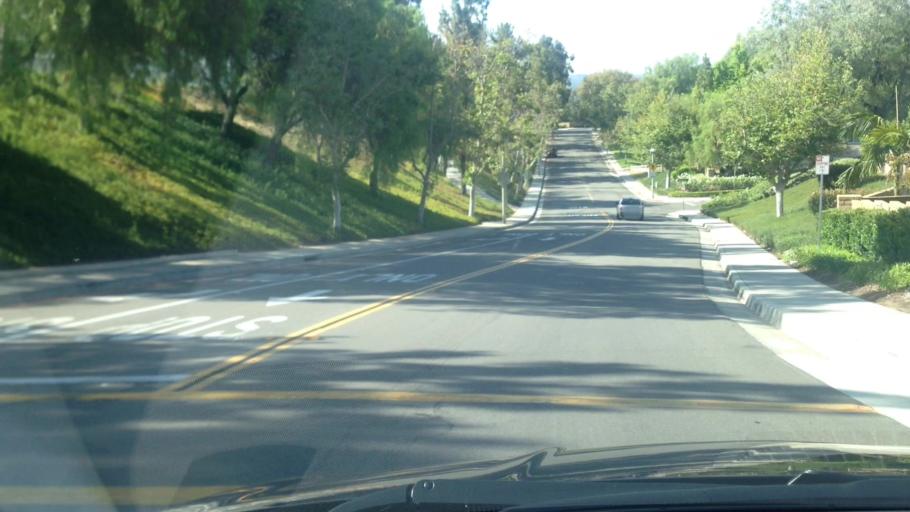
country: US
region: California
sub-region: Orange County
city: Yorba Linda
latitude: 33.8854
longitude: -117.7613
